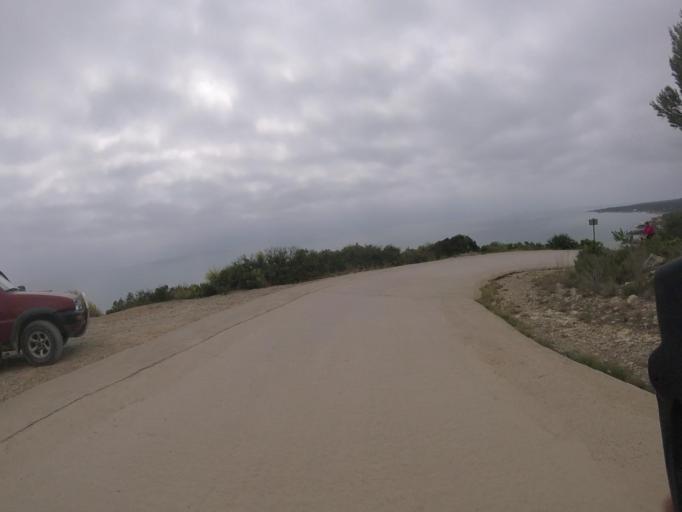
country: ES
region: Valencia
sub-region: Provincia de Castello
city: Peniscola
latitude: 40.3213
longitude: 0.3630
